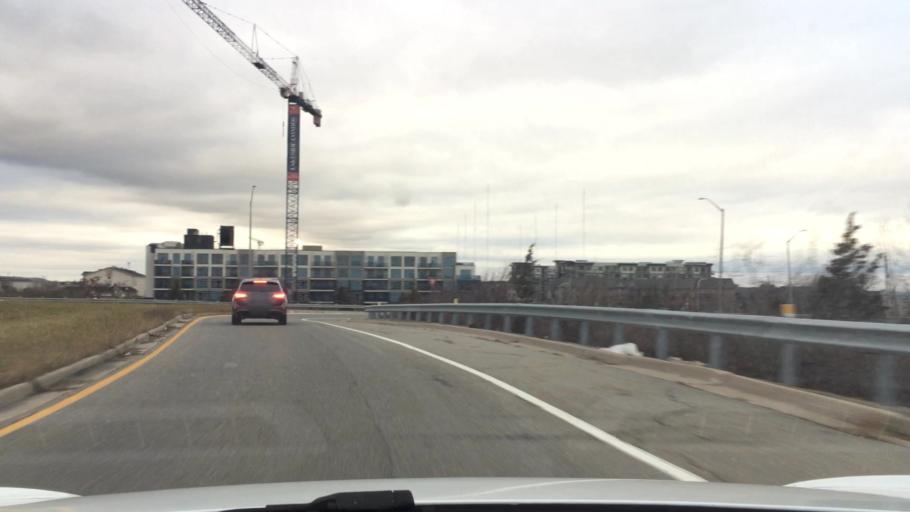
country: CA
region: Ontario
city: Oakville
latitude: 43.2086
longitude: -79.5947
